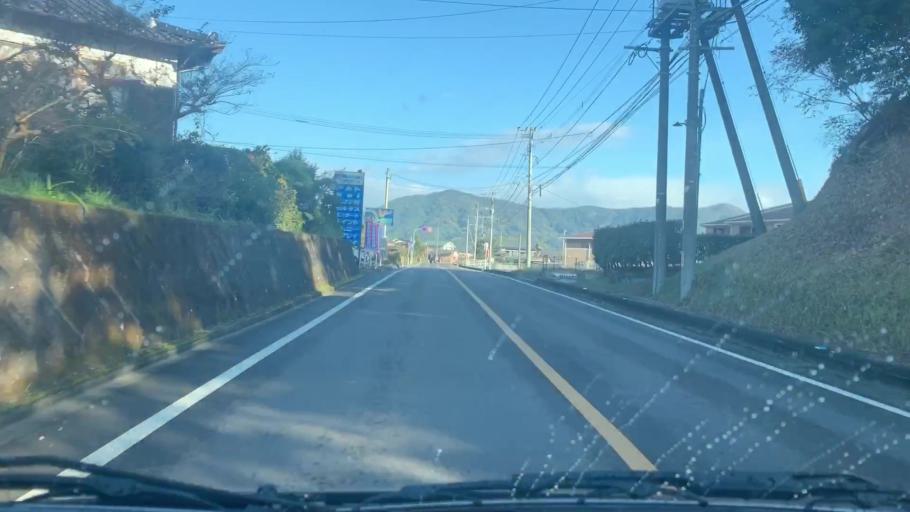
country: JP
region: Saga Prefecture
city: Takeocho-takeo
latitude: 33.2132
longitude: 130.0288
